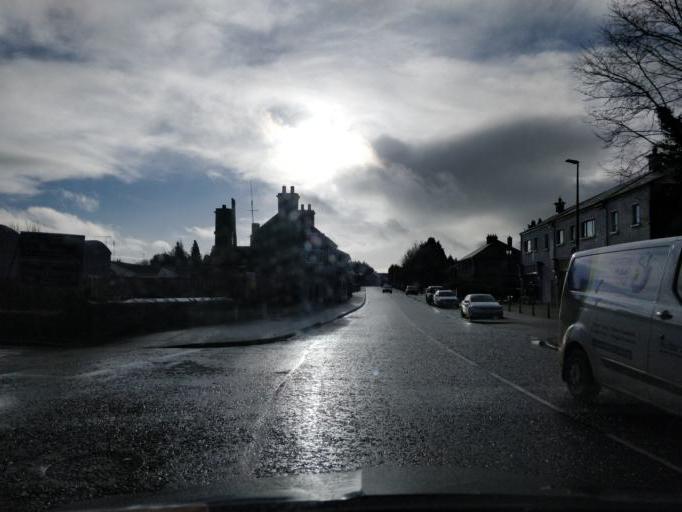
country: IE
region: Connaught
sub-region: Roscommon
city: Roscommon
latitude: 53.6370
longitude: -8.1907
